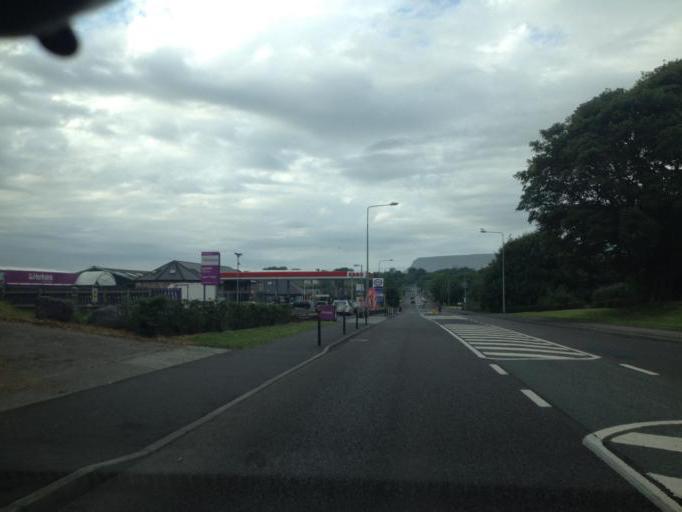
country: IE
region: Connaught
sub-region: Sligo
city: Sligo
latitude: 54.2819
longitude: -8.4723
